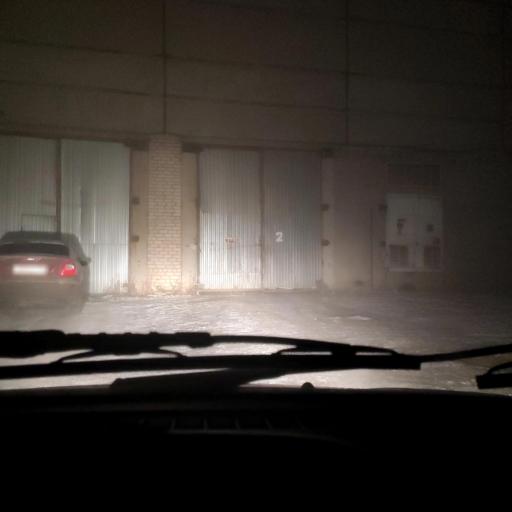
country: RU
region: Samara
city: Zhigulevsk
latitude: 53.4881
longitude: 49.4809
